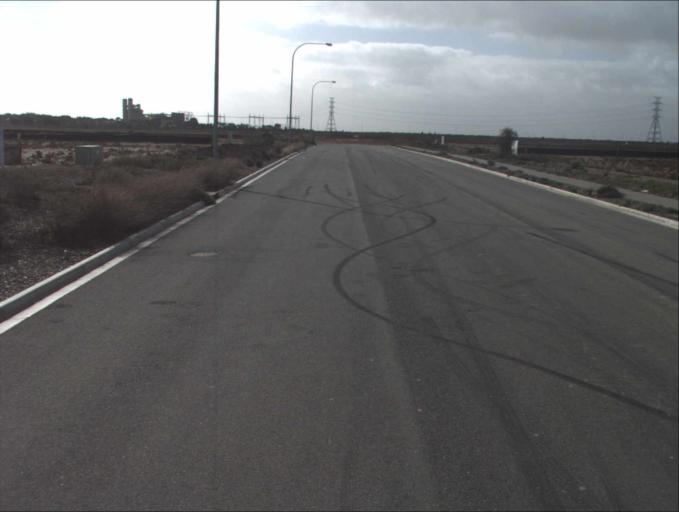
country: AU
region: South Australia
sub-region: Port Adelaide Enfield
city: Birkenhead
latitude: -34.7756
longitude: 138.5060
